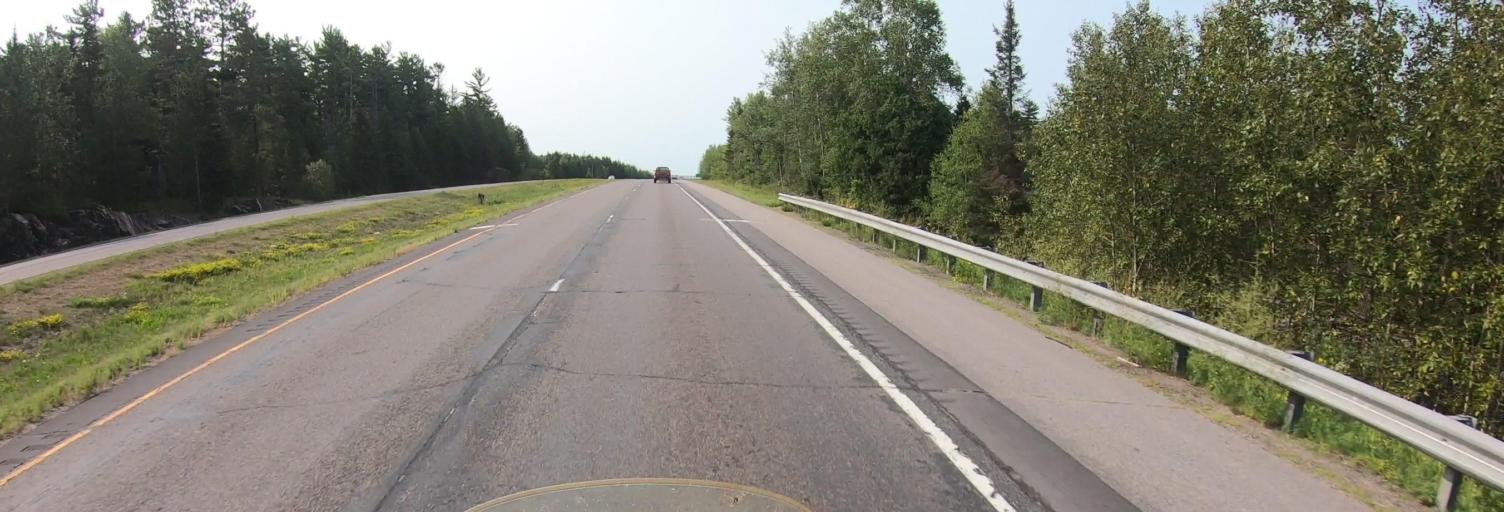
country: US
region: Minnesota
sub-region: Saint Louis County
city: Virginia
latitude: 47.5670
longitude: -92.5455
